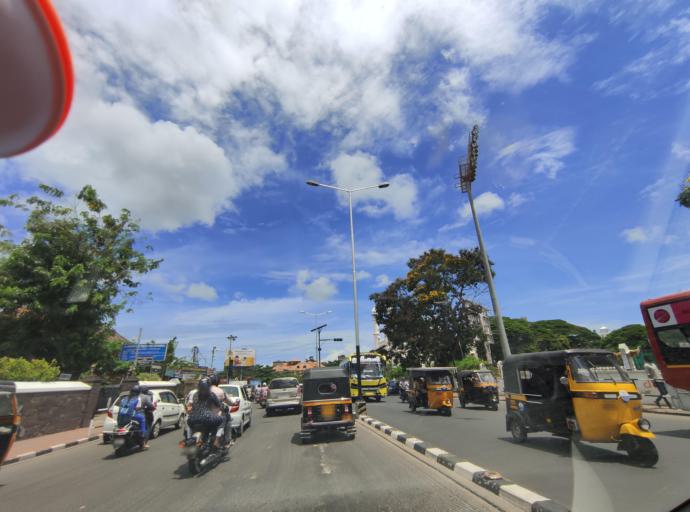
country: IN
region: Kerala
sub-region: Thiruvananthapuram
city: Thiruvananthapuram
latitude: 8.5043
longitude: 76.9512
